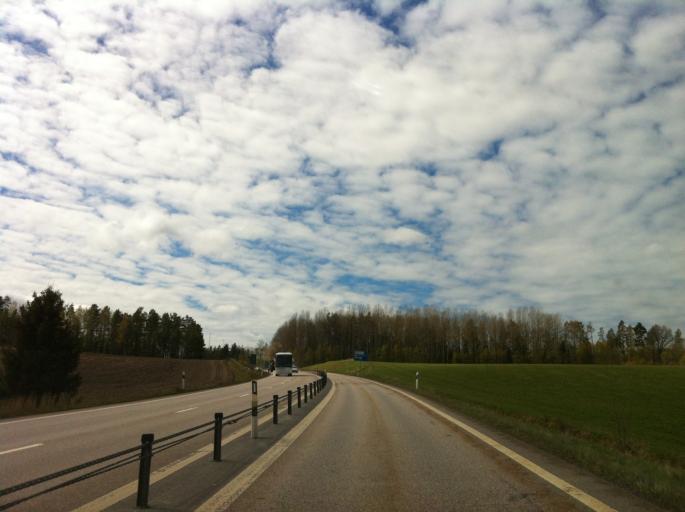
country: SE
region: OEstergoetland
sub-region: Valdemarsviks Kommun
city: Valdemarsvik
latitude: 58.1738
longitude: 16.5692
